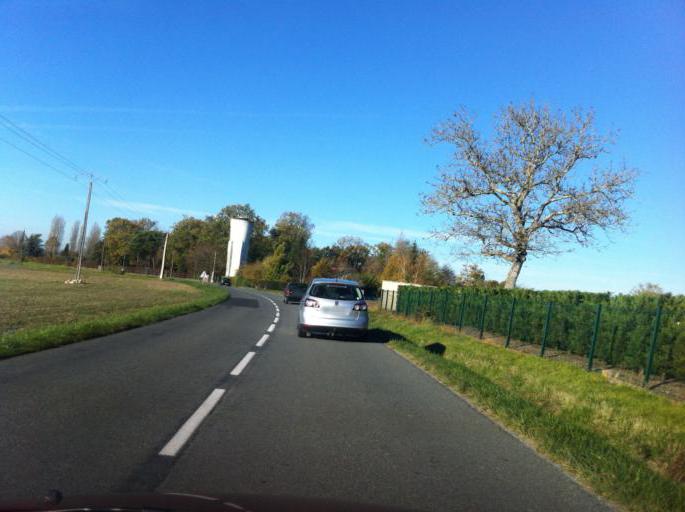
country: FR
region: Aquitaine
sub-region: Departement de la Dordogne
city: Saint-Aulaye
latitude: 45.2700
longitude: 0.1752
